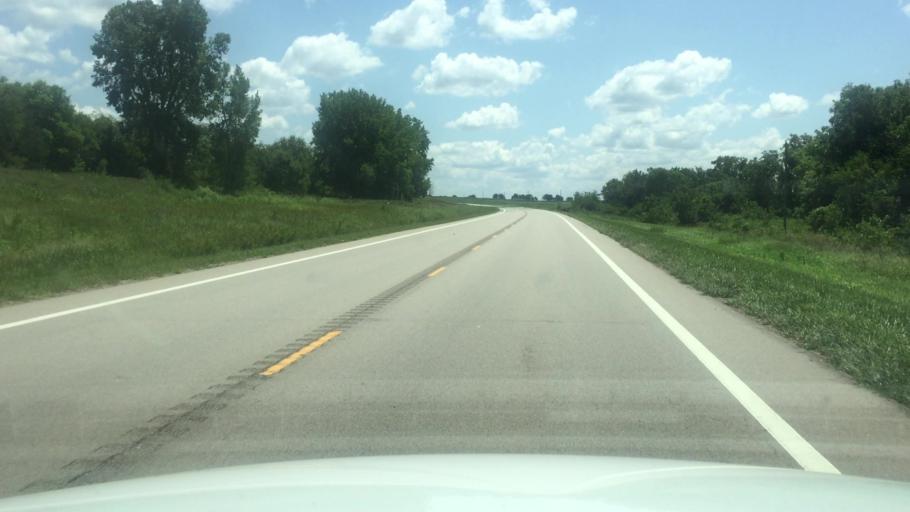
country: US
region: Kansas
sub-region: Brown County
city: Horton
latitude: 39.6191
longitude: -95.3490
